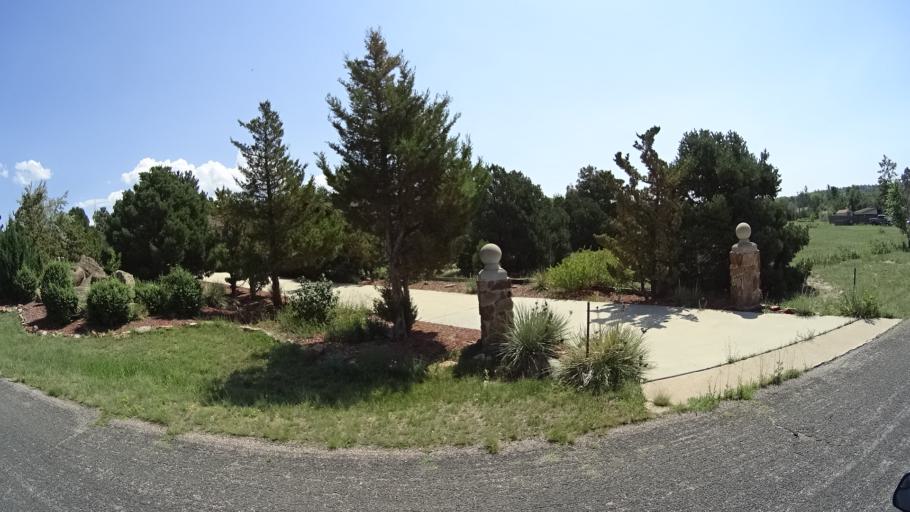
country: US
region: Colorado
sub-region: El Paso County
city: Air Force Academy
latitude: 38.9375
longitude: -104.7818
